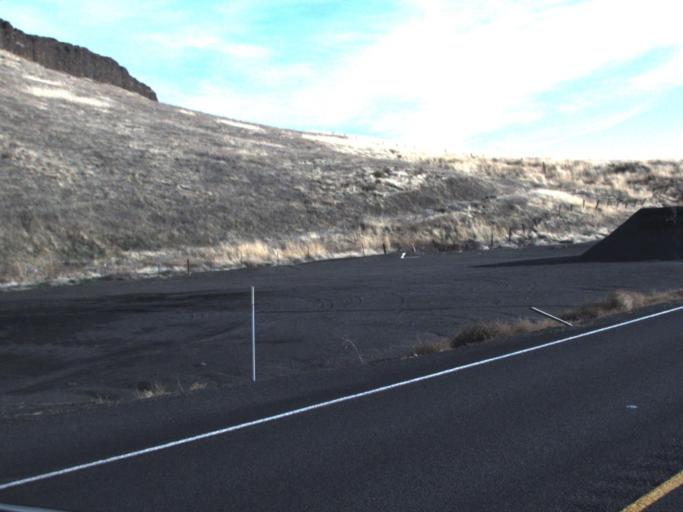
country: US
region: Washington
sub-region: Columbia County
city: Dayton
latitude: 46.4958
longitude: -117.9715
